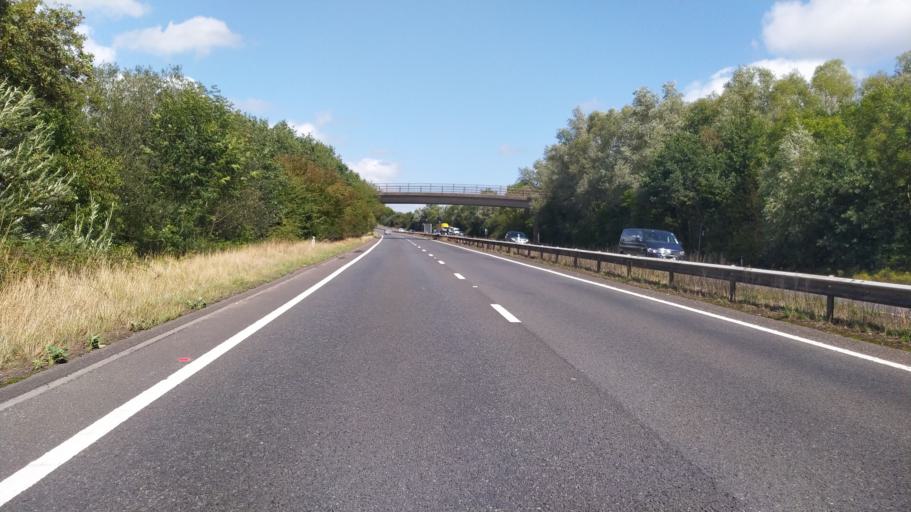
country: GB
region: England
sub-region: Hampshire
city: Liss
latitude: 51.0407
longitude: -0.9034
